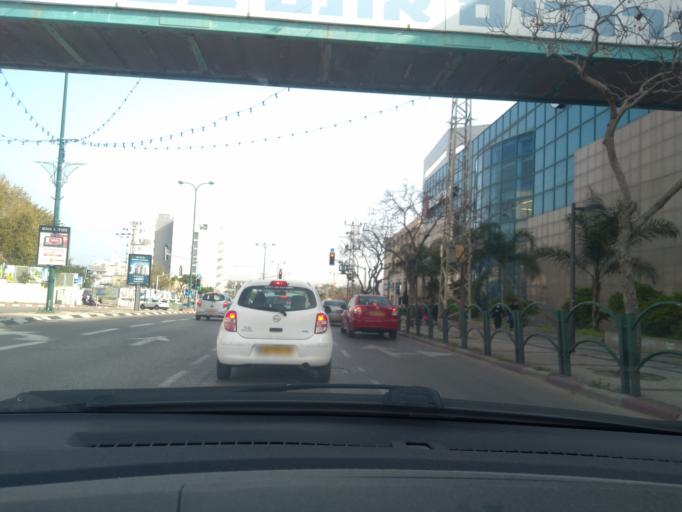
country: IL
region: Central District
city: Netanya
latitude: 32.3268
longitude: 34.8619
